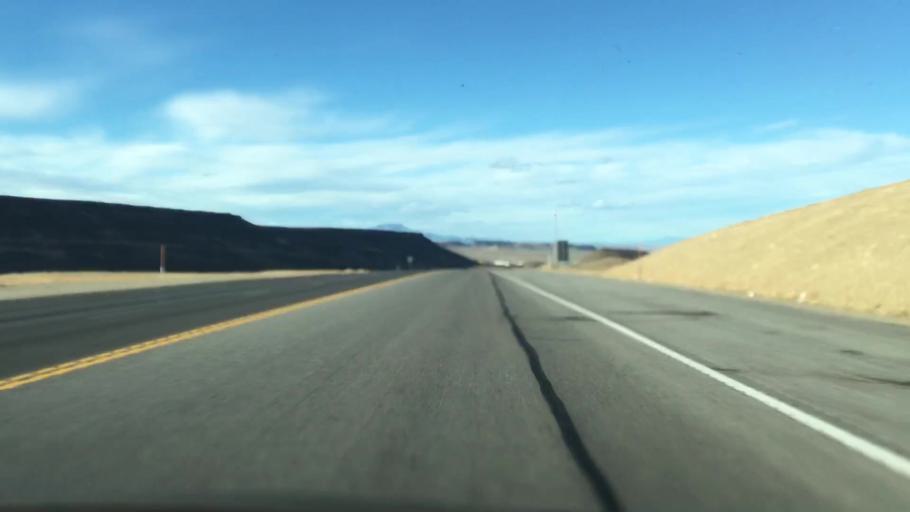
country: US
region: Nevada
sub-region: Esmeralda County
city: Goldfield
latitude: 37.6815
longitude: -117.2291
